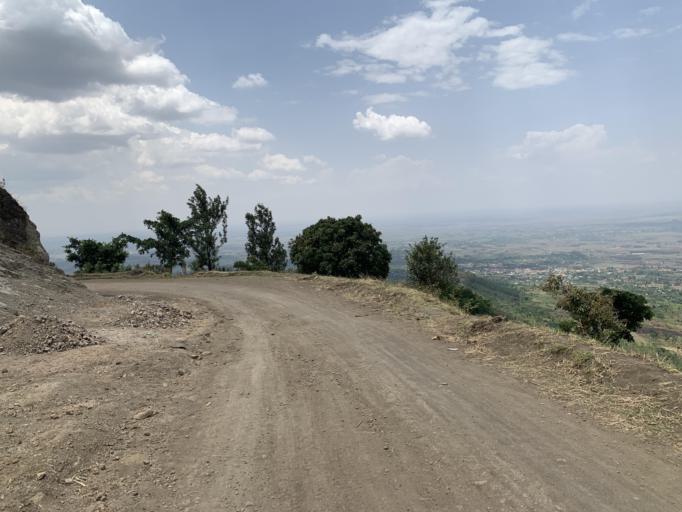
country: UG
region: Eastern Region
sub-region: Sironko District
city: Sironko
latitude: 1.2627
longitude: 34.2979
